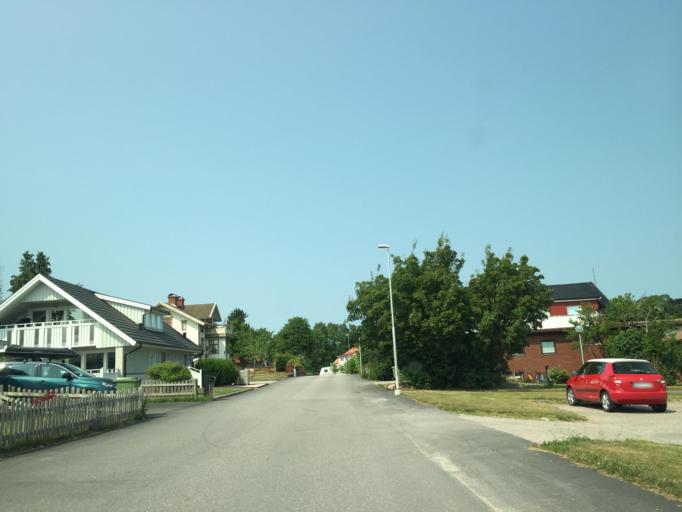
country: SE
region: Vaestra Goetaland
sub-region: Lilla Edets Kommun
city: Lilla Edet
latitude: 58.1795
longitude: 12.1084
